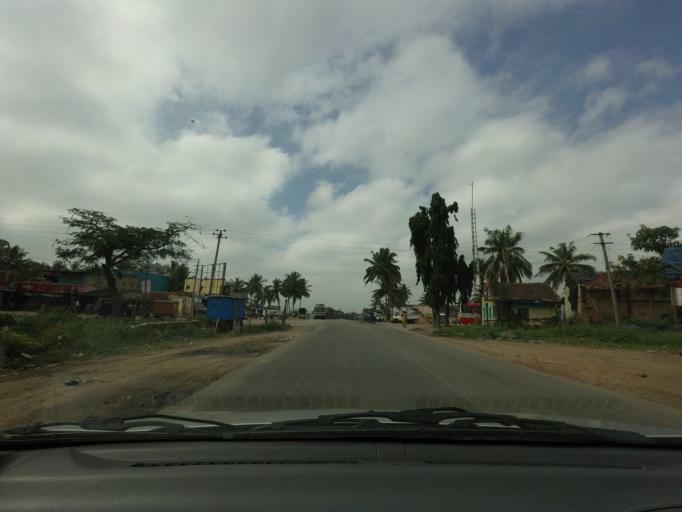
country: IN
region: Karnataka
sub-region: Hassan
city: Alur
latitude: 12.9601
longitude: 75.9854
